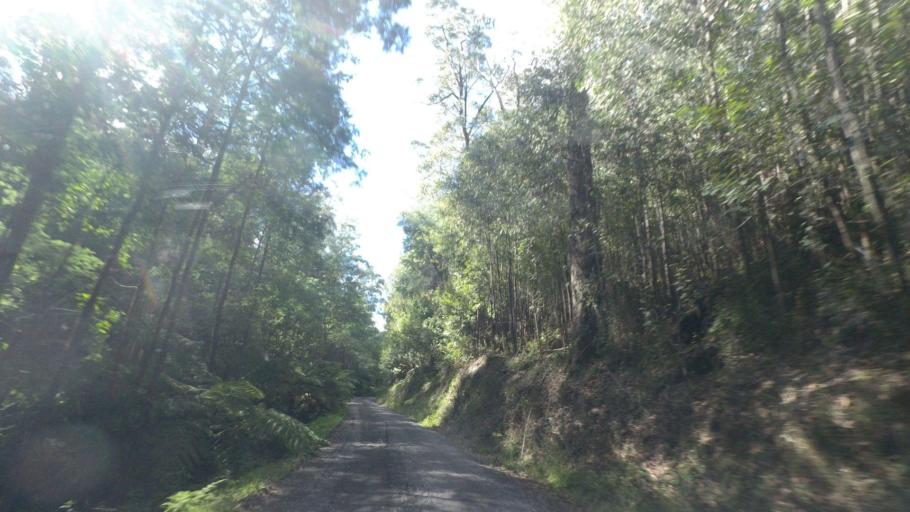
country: AU
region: Victoria
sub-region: Cardinia
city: Bunyip
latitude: -37.9586
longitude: 145.8198
